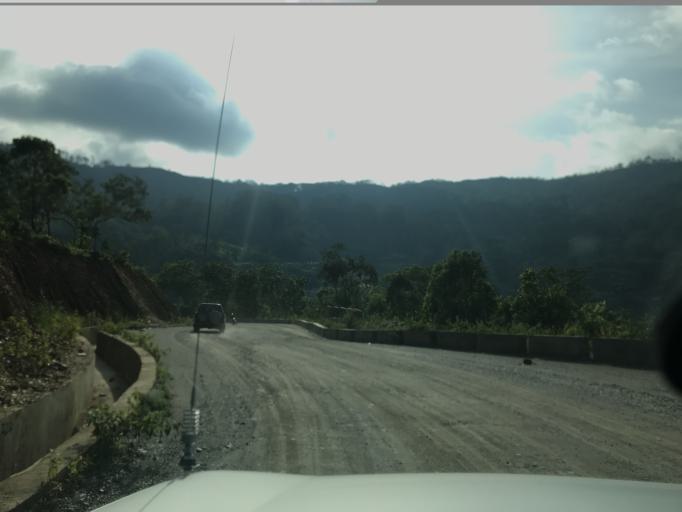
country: TL
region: Aileu
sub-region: Aileu Villa
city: Aileu
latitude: -8.6640
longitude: 125.5457
